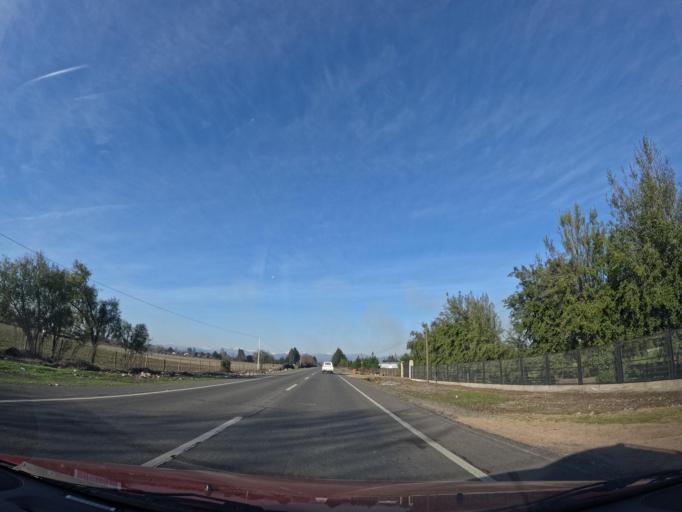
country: CL
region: Maule
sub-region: Provincia de Talca
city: San Clemente
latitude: -35.6274
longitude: -71.4691
